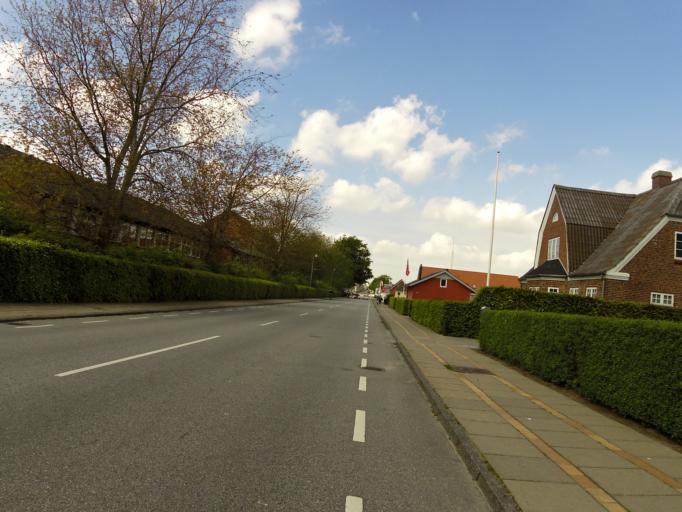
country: DK
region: South Denmark
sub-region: Tonder Kommune
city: Toftlund
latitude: 55.1869
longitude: 9.0659
